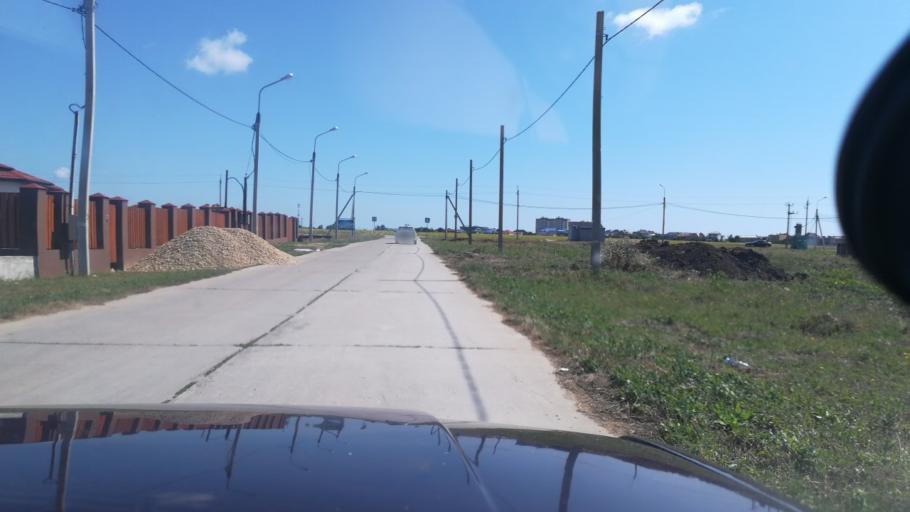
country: RU
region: Krasnodarskiy
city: Vityazevo
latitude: 44.9894
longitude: 37.2756
